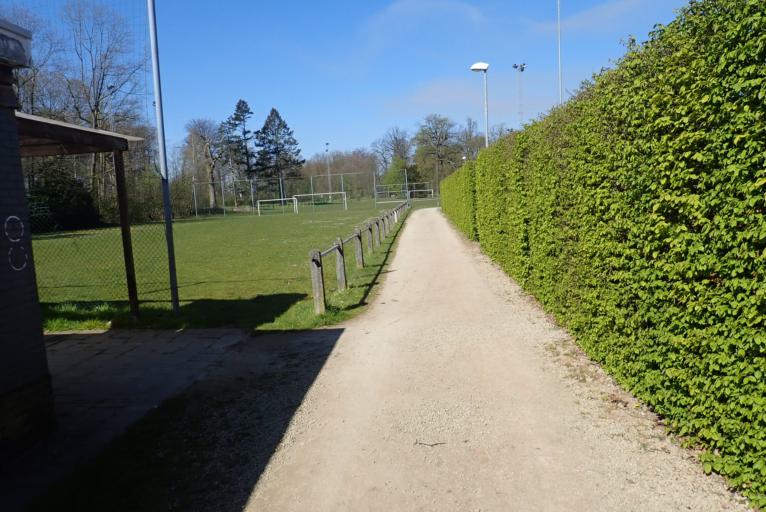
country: BE
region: Flanders
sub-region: Provincie Antwerpen
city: Schoten
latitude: 51.2438
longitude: 4.4929
